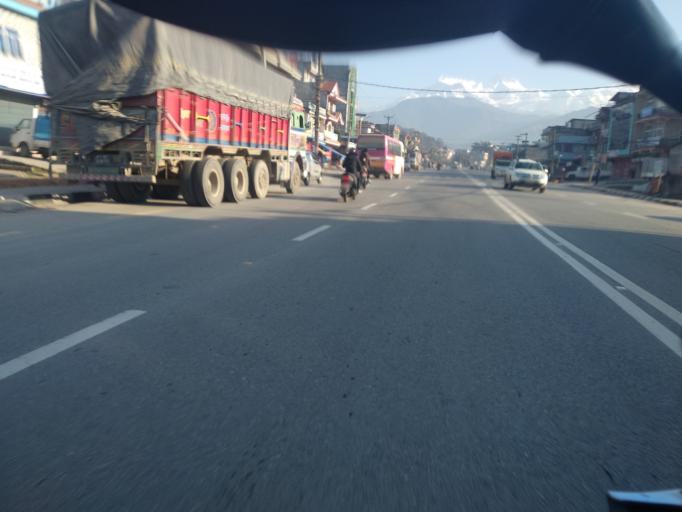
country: NP
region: Western Region
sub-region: Gandaki Zone
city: Pokhara
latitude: 28.2207
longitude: 83.9779
